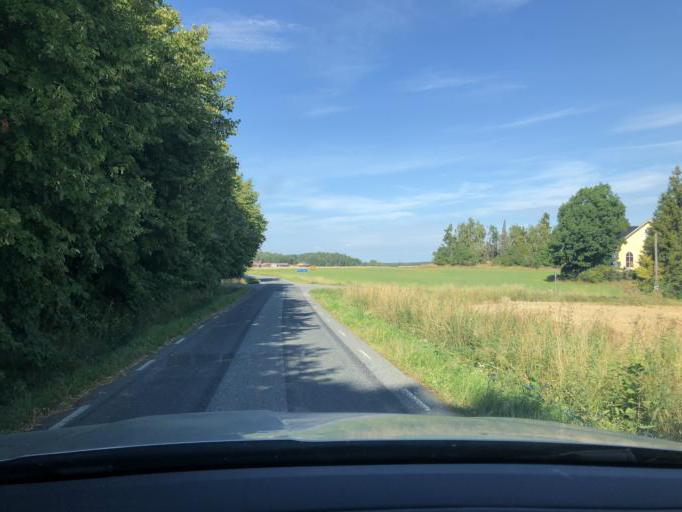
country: SE
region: Uppsala
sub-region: Enkopings Kommun
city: Irsta
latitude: 59.7421
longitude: 16.9406
